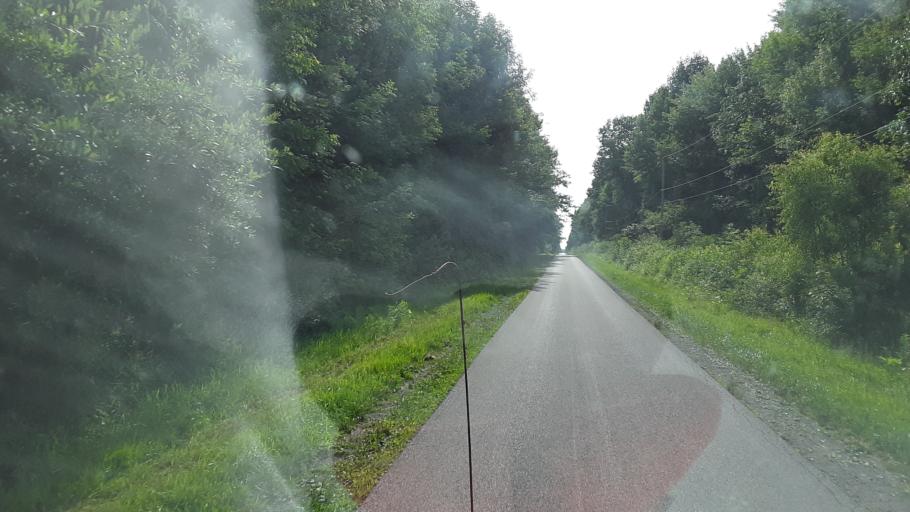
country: US
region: Ohio
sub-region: Ashtabula County
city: Andover
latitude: 41.6908
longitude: -80.6167
